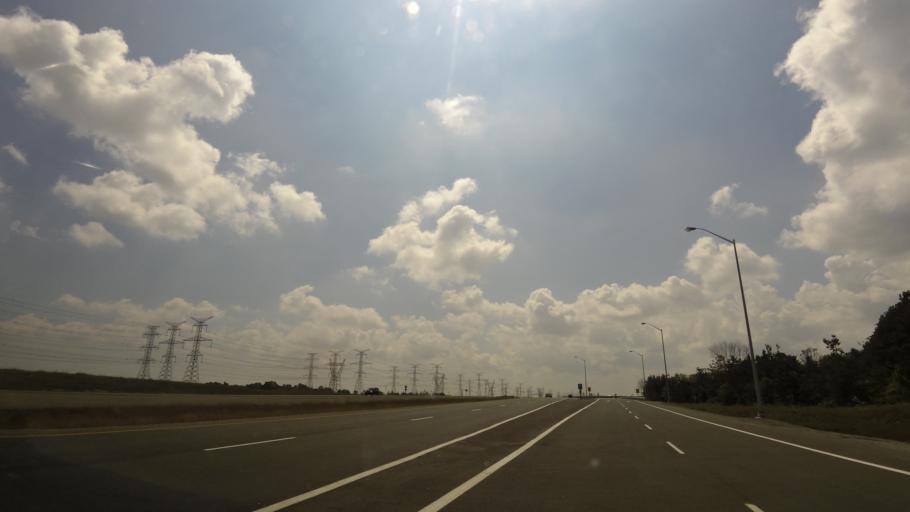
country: CA
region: Ontario
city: Oshawa
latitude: 43.9557
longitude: -78.9327
